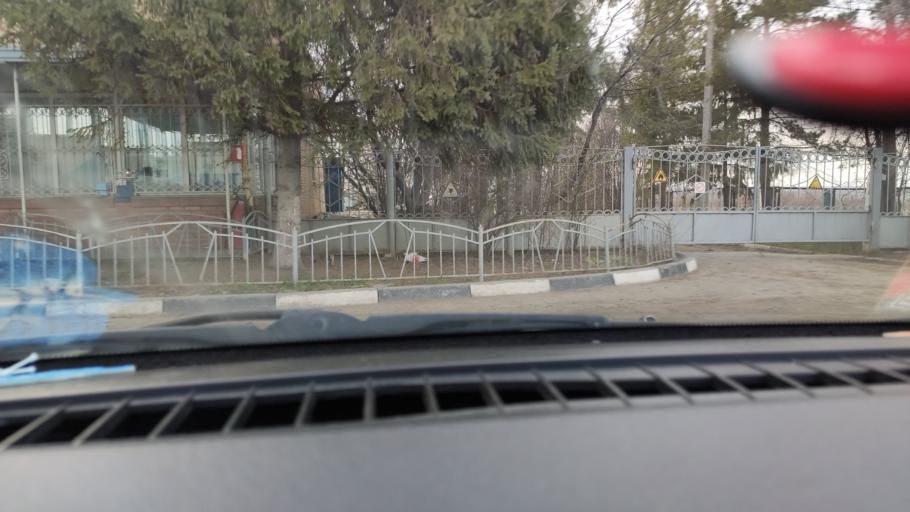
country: RU
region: Saratov
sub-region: Saratovskiy Rayon
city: Saratov
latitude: 51.6185
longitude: 45.9469
